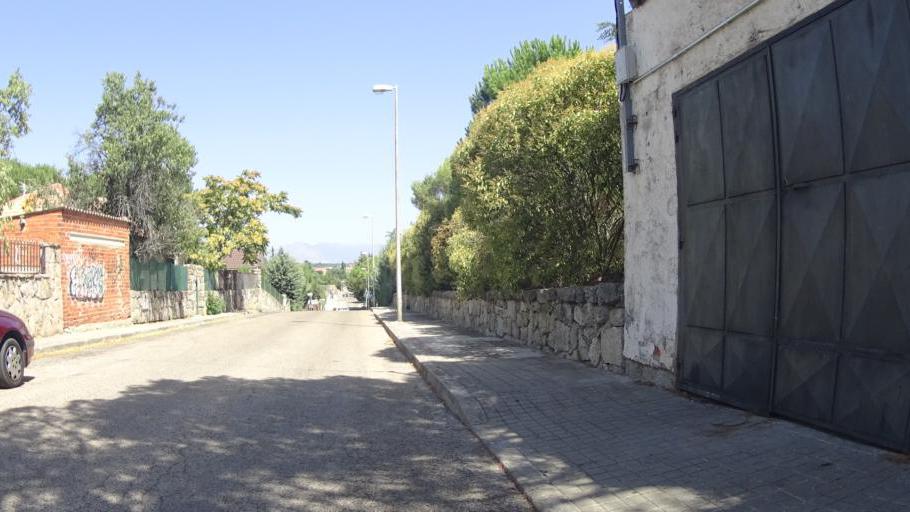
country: ES
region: Madrid
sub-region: Provincia de Madrid
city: Colmenarejo
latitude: 40.5602
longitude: -4.0130
